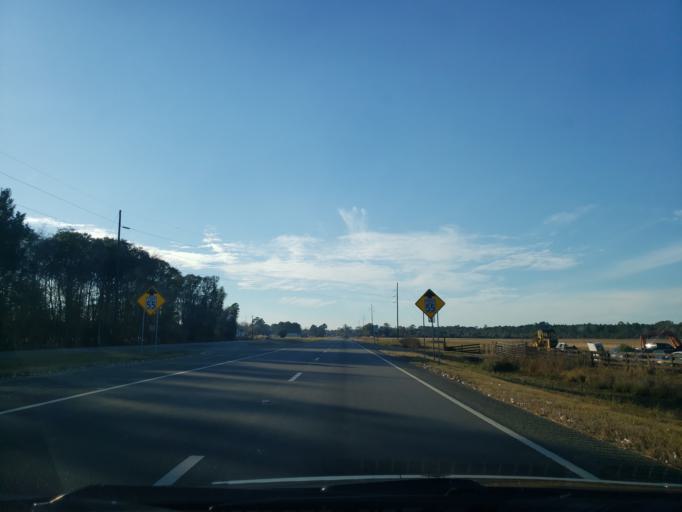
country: US
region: Georgia
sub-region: Atkinson County
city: Pearson
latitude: 31.2952
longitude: -82.8344
